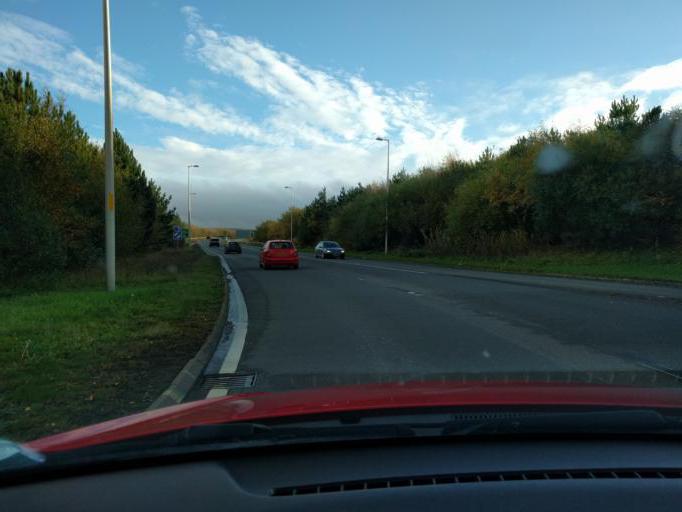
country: GB
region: Scotland
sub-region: The Scottish Borders
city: Duns
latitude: 55.9396
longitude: -2.3612
